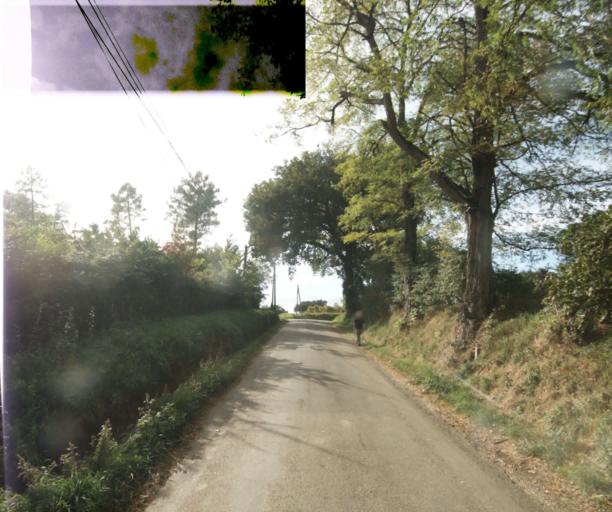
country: FR
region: Midi-Pyrenees
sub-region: Departement du Gers
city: Gondrin
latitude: 43.8748
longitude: 0.2388
